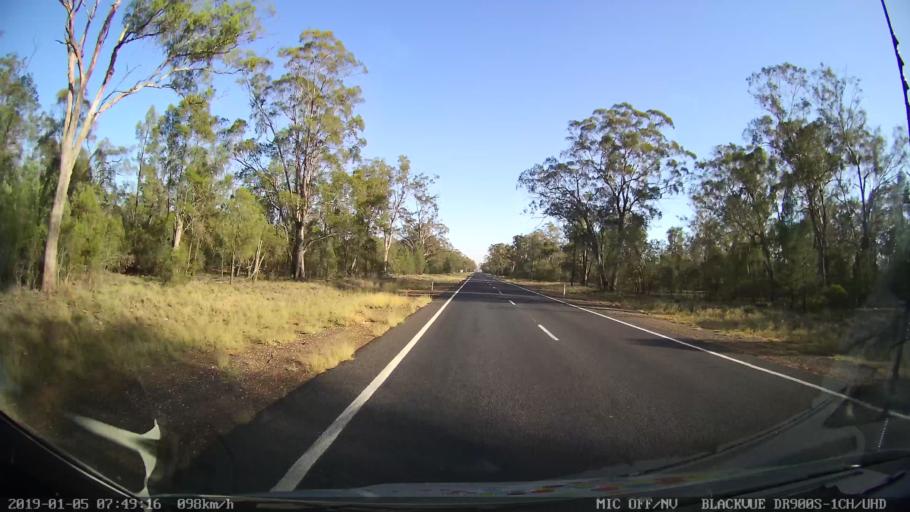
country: AU
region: New South Wales
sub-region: Gilgandra
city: Gilgandra
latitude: -31.8042
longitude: 148.6365
